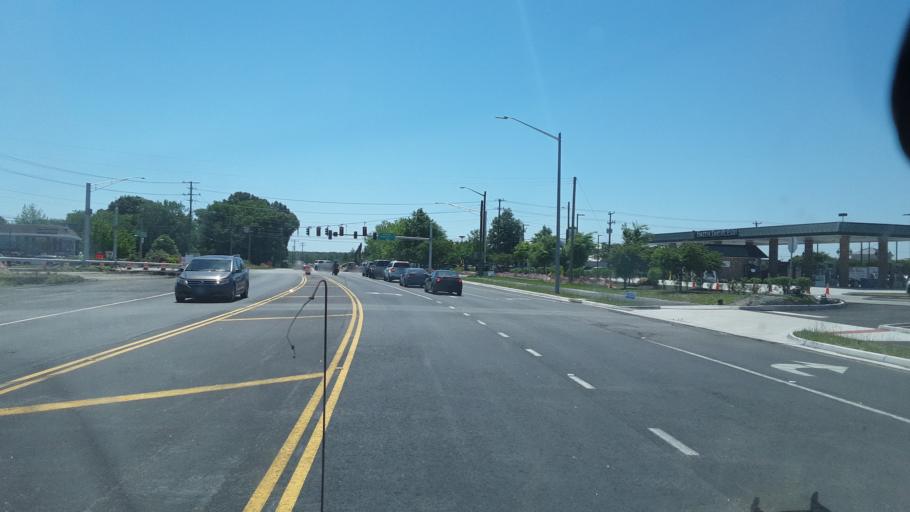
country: US
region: Virginia
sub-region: City of Virginia Beach
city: Virginia Beach
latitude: 36.7528
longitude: -76.0108
